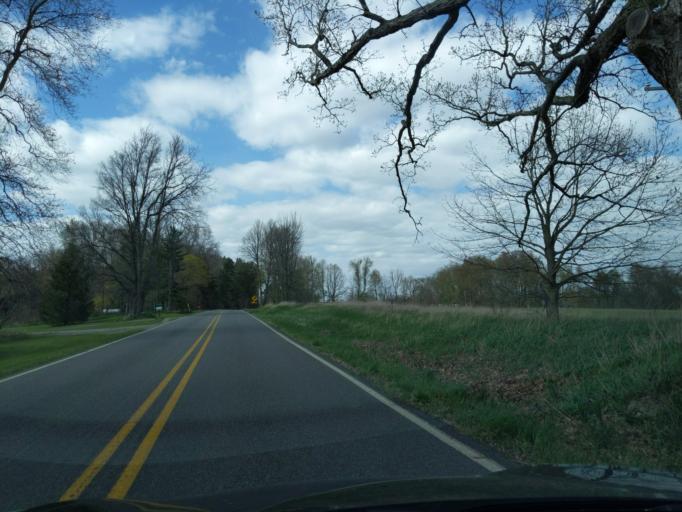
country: US
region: Michigan
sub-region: Ingham County
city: Leslie
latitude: 42.4189
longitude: -84.5415
